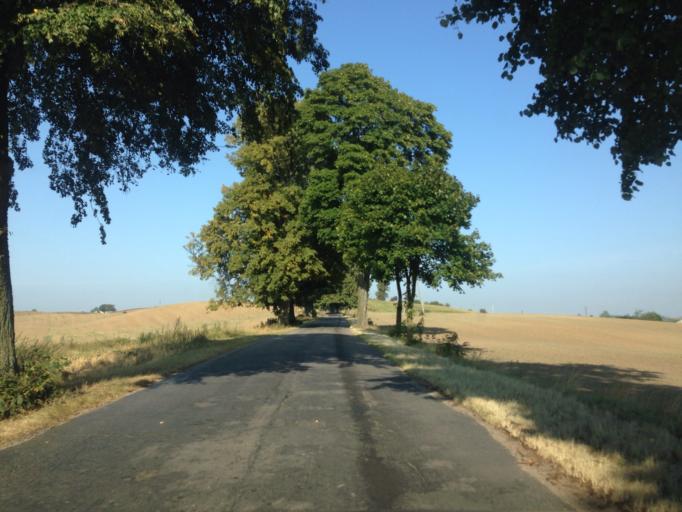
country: PL
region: Kujawsko-Pomorskie
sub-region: Powiat brodnicki
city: Brzozie
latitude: 53.2942
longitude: 19.6720
